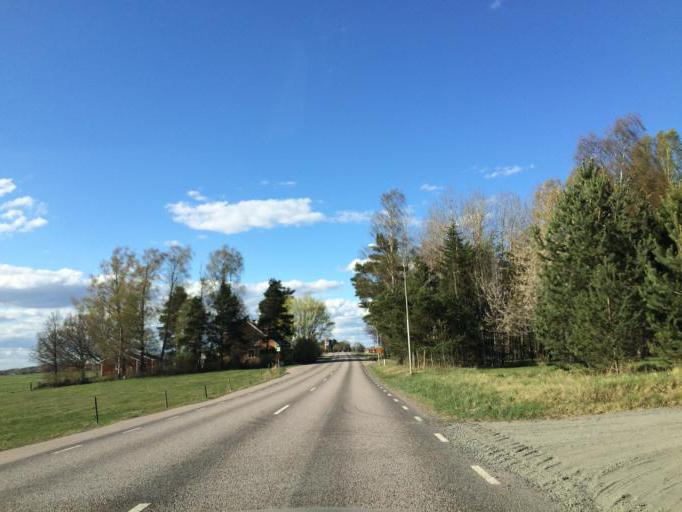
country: SE
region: Soedermanland
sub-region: Eskilstuna Kommun
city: Kvicksund
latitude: 59.4173
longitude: 16.3423
